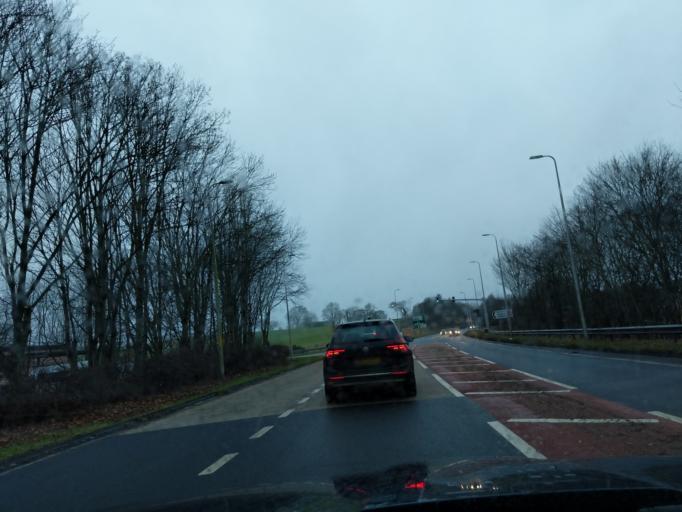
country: GB
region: Scotland
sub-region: The Scottish Borders
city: Melrose
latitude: 55.5981
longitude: -2.7438
